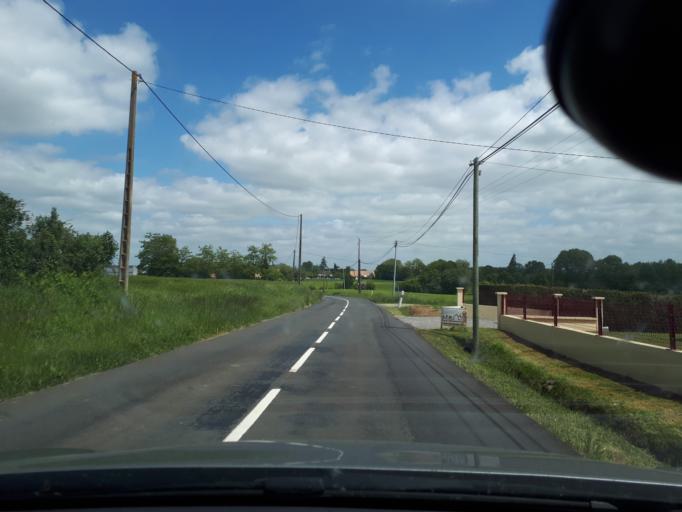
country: FR
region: Pays de la Loire
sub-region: Departement de la Sarthe
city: Change
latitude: 48.0326
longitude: 0.2844
